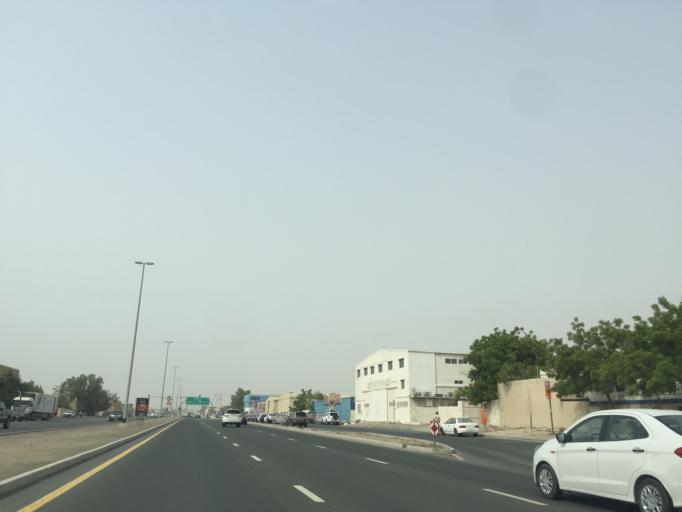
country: AE
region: Dubai
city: Dubai
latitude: 25.1167
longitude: 55.2219
